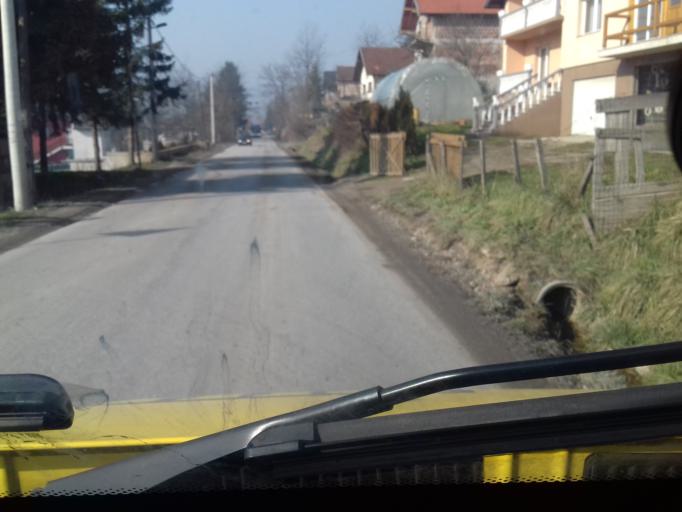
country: BA
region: Federation of Bosnia and Herzegovina
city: Ilijas
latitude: 43.9436
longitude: 18.2725
